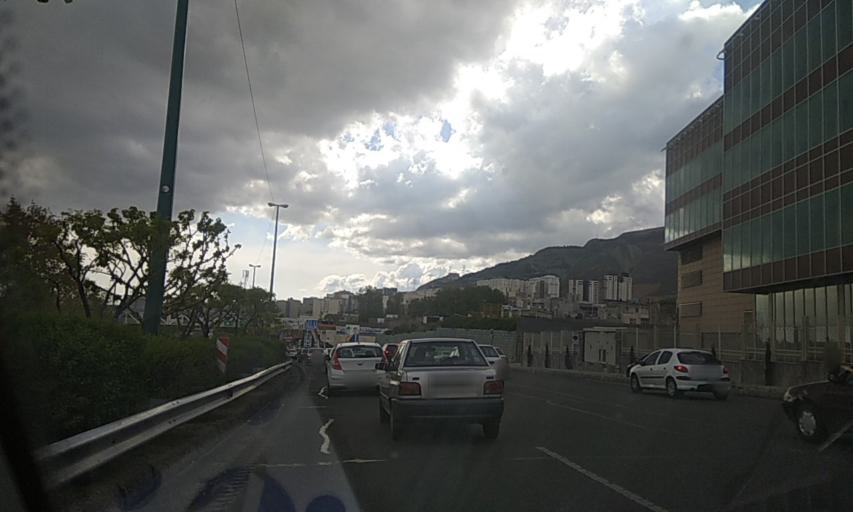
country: IR
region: Tehran
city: Tajrish
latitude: 35.7848
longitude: 51.3487
